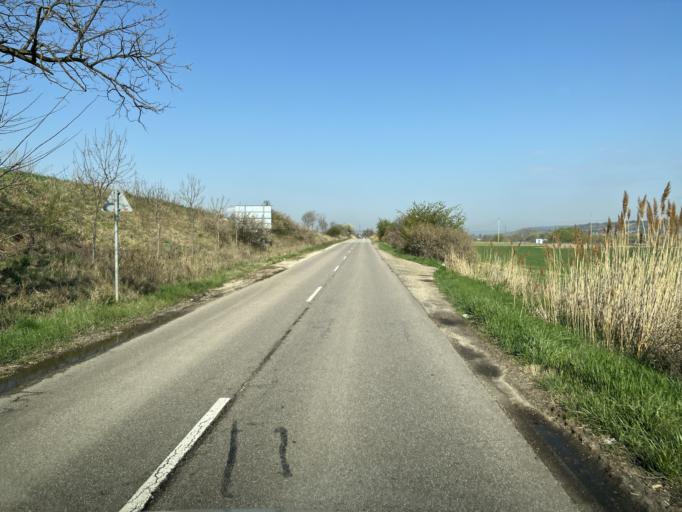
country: HU
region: Pest
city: Aszod
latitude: 47.6440
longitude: 19.4607
